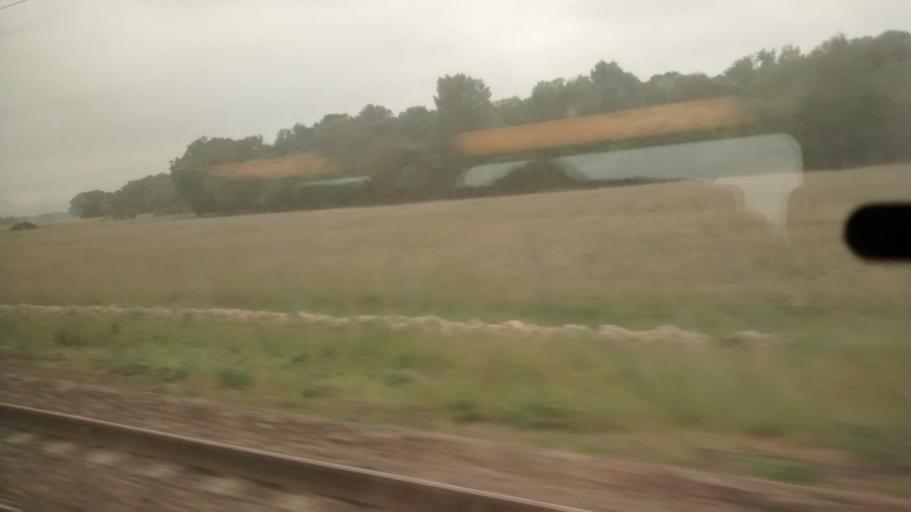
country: FR
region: Ile-de-France
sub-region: Departement de Seine-et-Marne
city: Le Chatelet-en-Brie
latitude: 48.5193
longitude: 2.8208
